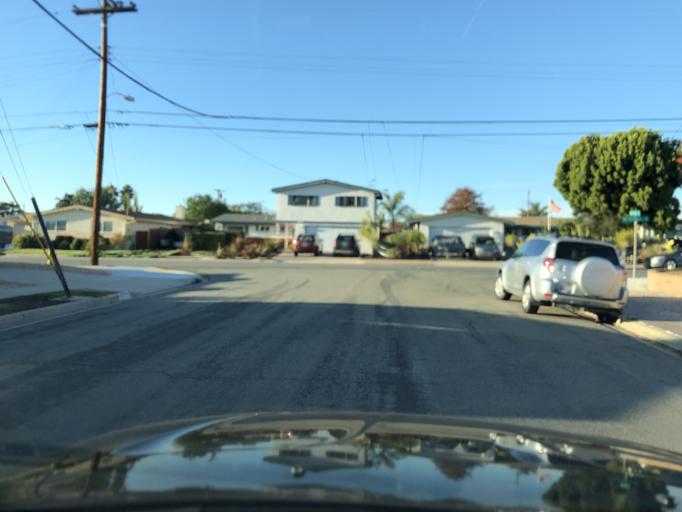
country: US
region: California
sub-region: San Diego County
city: La Jolla
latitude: 32.8186
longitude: -117.1969
